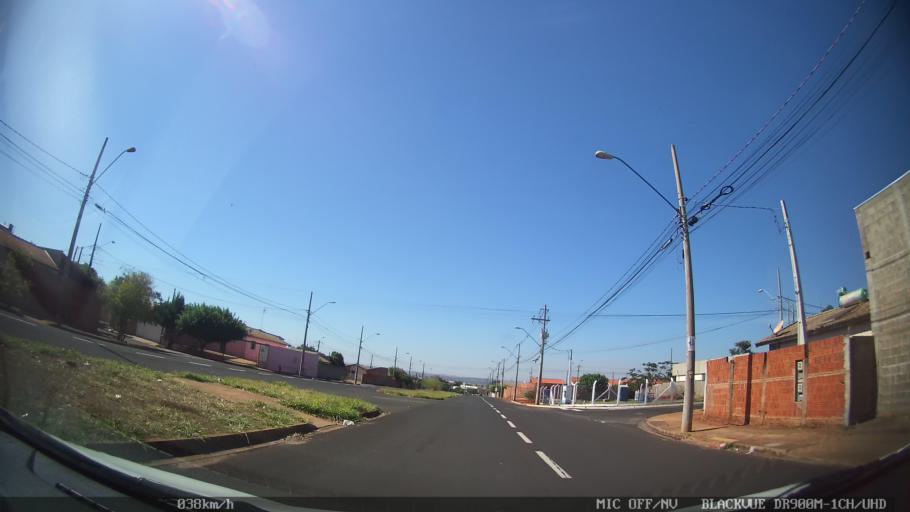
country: BR
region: Sao Paulo
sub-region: Sao Jose Do Rio Preto
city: Sao Jose do Rio Preto
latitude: -20.7406
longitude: -49.4135
